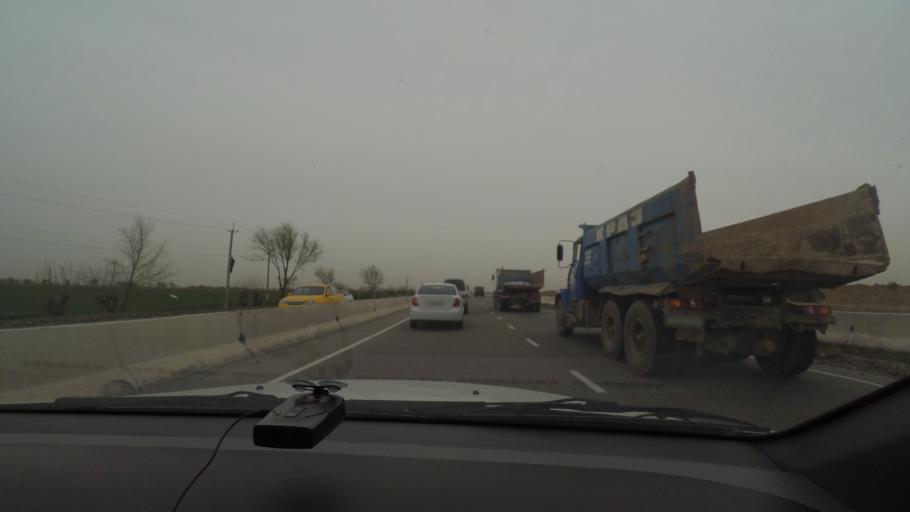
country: UZ
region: Jizzax
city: Gagarin
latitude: 40.4524
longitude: 68.2514
